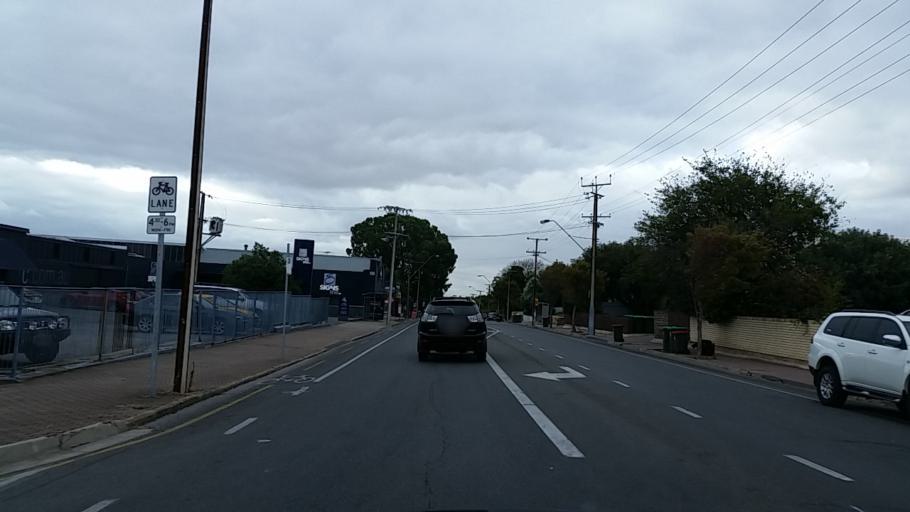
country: AU
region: South Australia
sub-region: Prospect
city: Prospect
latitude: -34.8773
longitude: 138.5933
